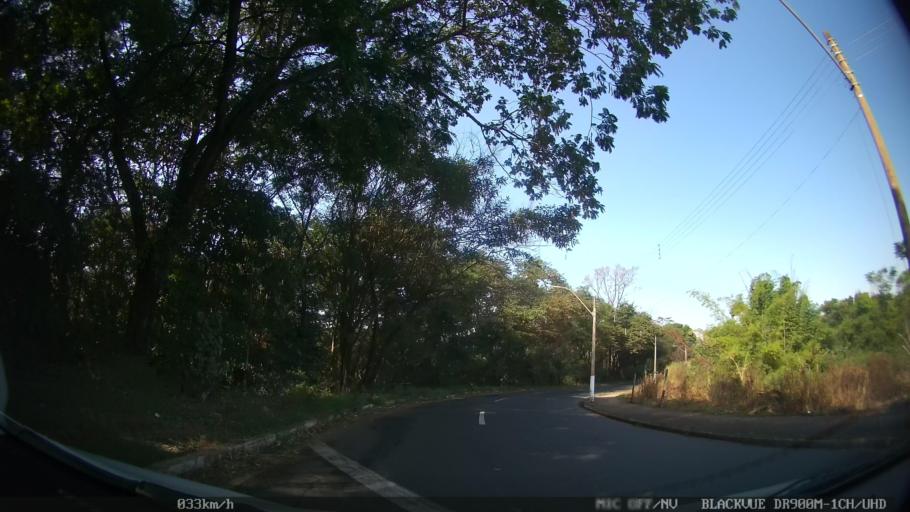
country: BR
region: Sao Paulo
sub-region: Americana
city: Americana
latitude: -22.7233
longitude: -47.3283
